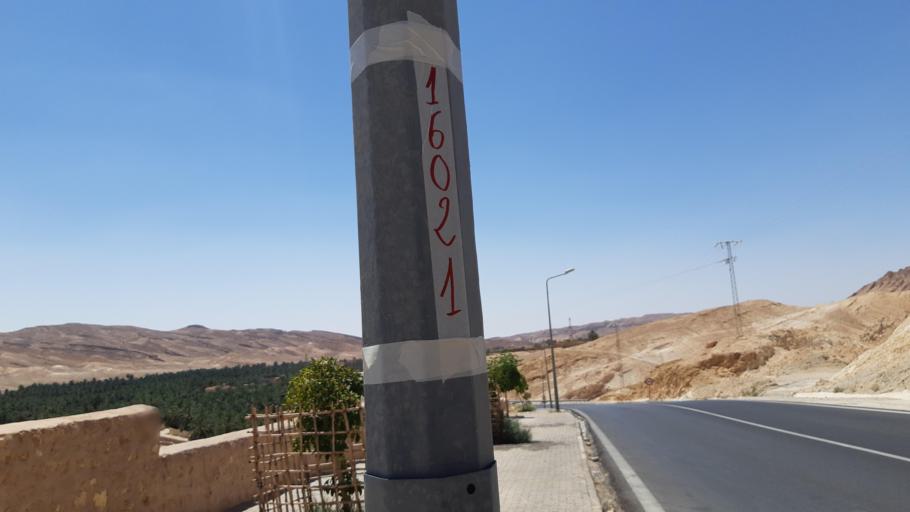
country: TN
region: Tawzar
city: Tamaghzah
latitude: 34.3906
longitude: 7.9481
